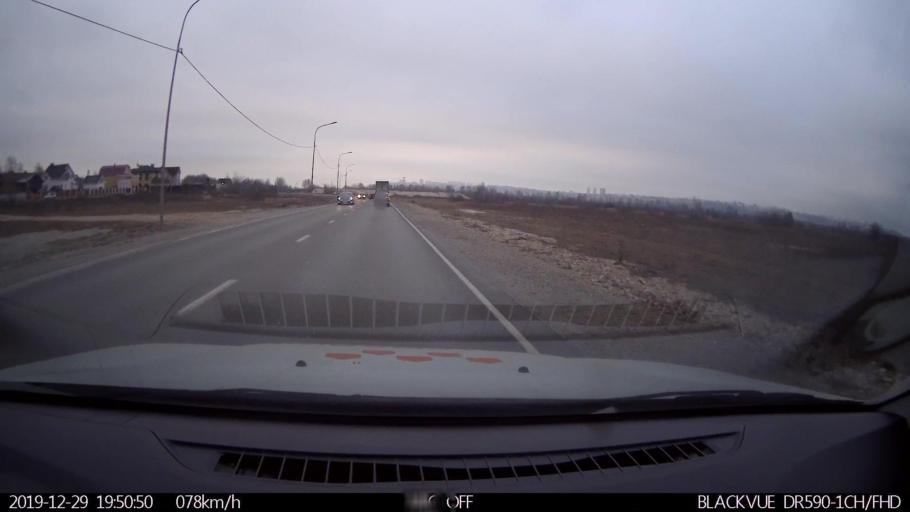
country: RU
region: Nizjnij Novgorod
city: Bor
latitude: 56.3637
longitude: 44.0324
